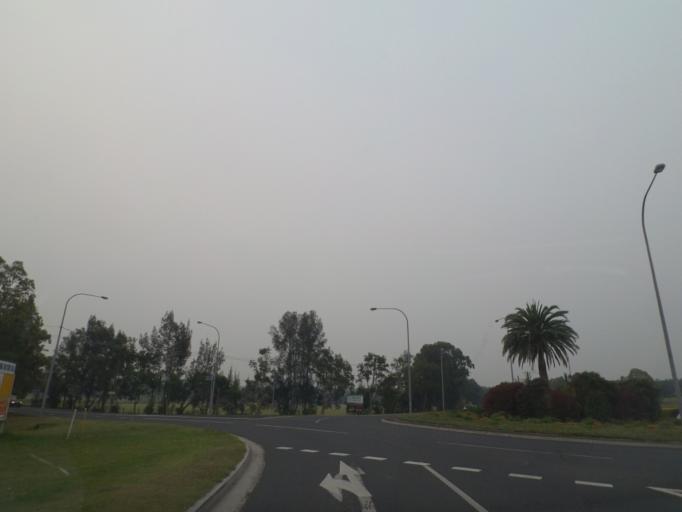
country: AU
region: New South Wales
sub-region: Coffs Harbour
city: Toormina
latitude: -30.3262
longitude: 153.0985
